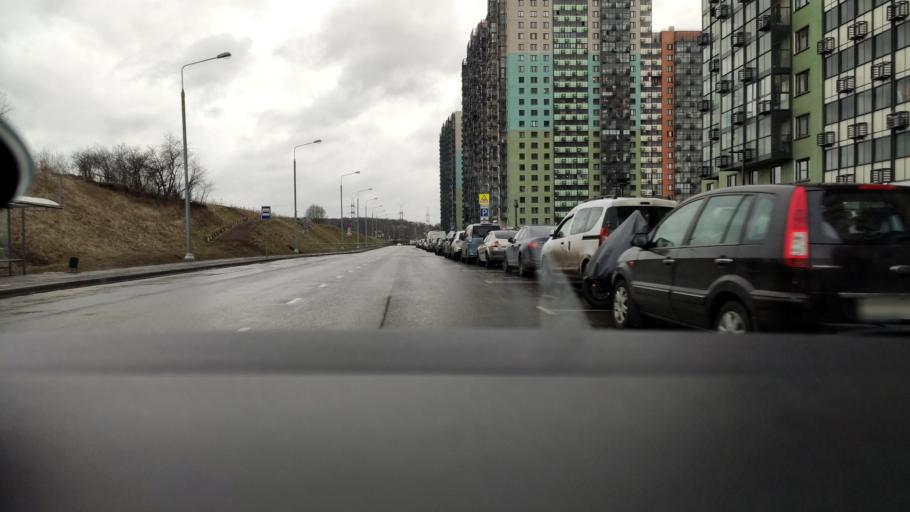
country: RU
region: Moskovskaya
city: Pavshino
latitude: 55.8605
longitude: 37.3719
